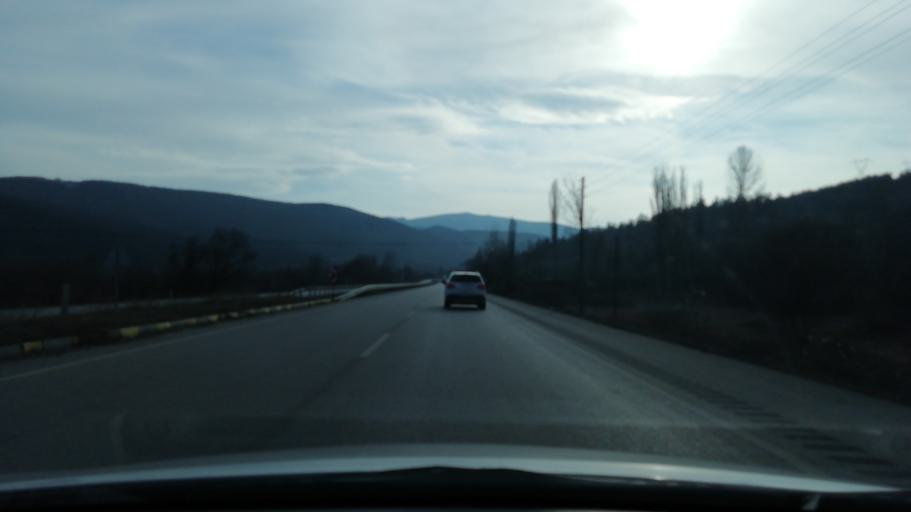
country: TR
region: Karabuk
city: Eskipazar
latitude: 41.0184
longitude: 32.6263
